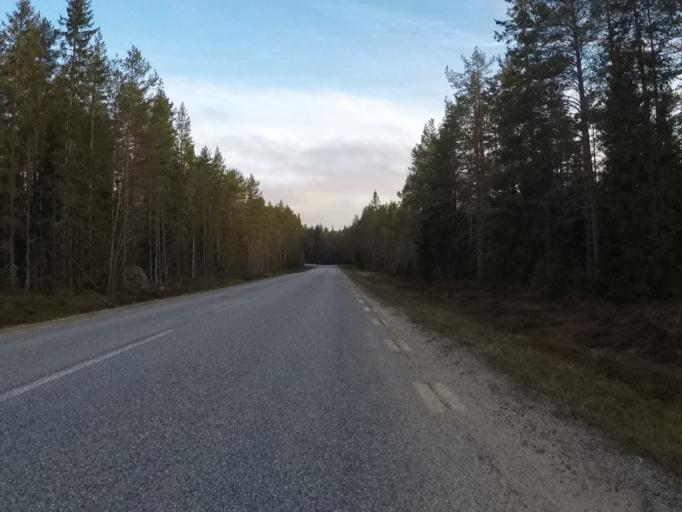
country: SE
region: Vaesterbotten
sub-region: Robertsfors Kommun
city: Robertsfors
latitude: 63.9829
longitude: 20.8116
